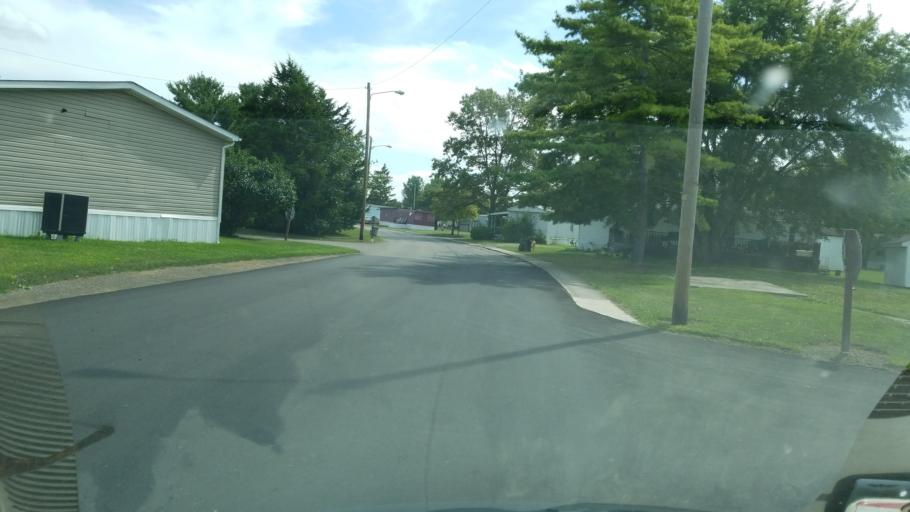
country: US
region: Ohio
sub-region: Marion County
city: Marion
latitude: 40.5326
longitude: -83.1017
